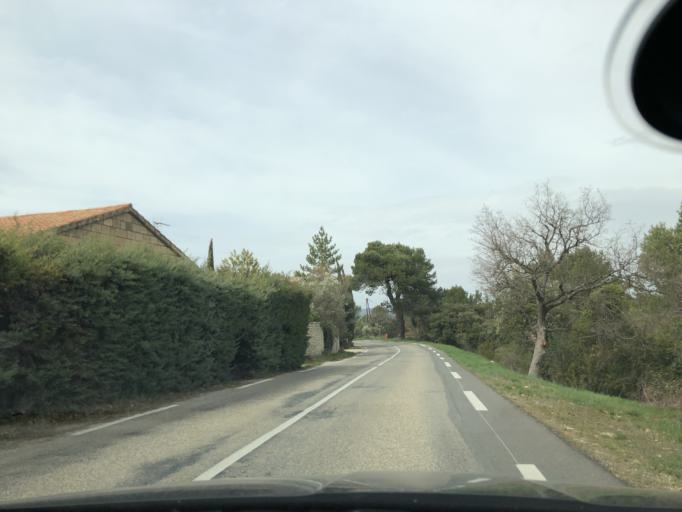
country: FR
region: Provence-Alpes-Cote d'Azur
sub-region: Departement du Vaucluse
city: Goult
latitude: 43.8332
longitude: 5.2377
